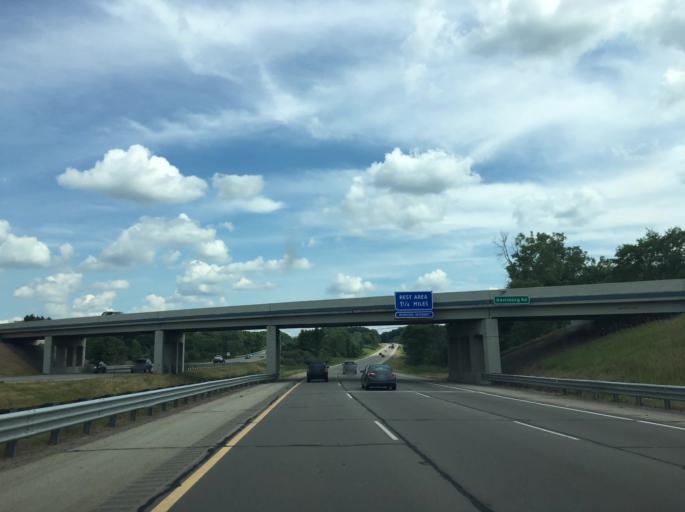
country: US
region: Michigan
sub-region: Oakland County
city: Clarkston
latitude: 42.7589
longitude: -83.5072
